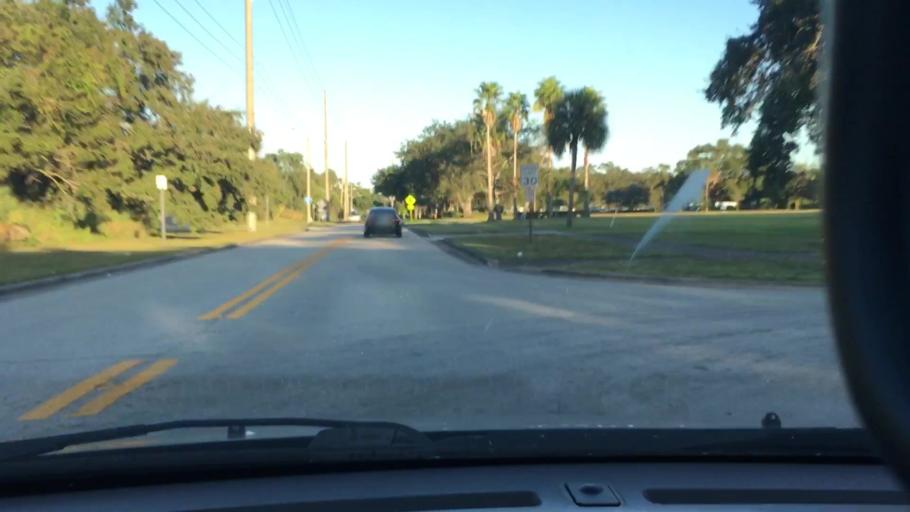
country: US
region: Florida
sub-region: Indian River County
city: Vero Beach
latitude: 27.6456
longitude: -80.4054
